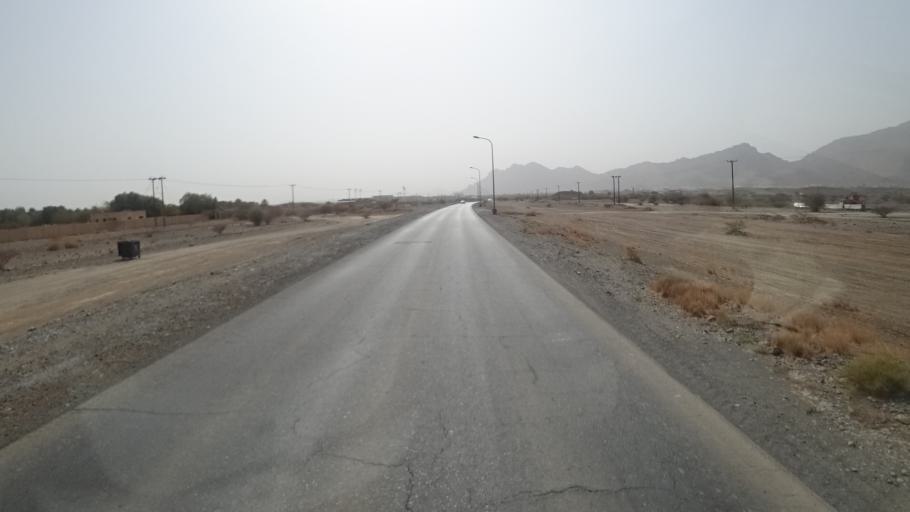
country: OM
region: Muhafazat ad Dakhiliyah
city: Nizwa
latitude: 22.9143
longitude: 57.6053
